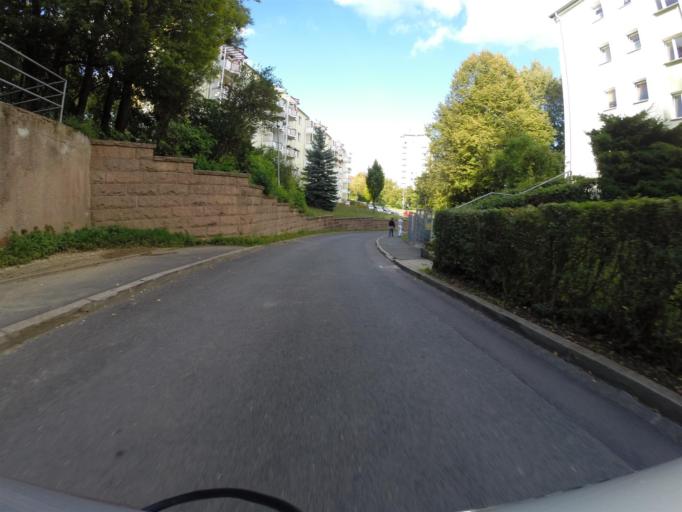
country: DE
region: Thuringia
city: Jena
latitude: 50.9501
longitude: 11.6001
